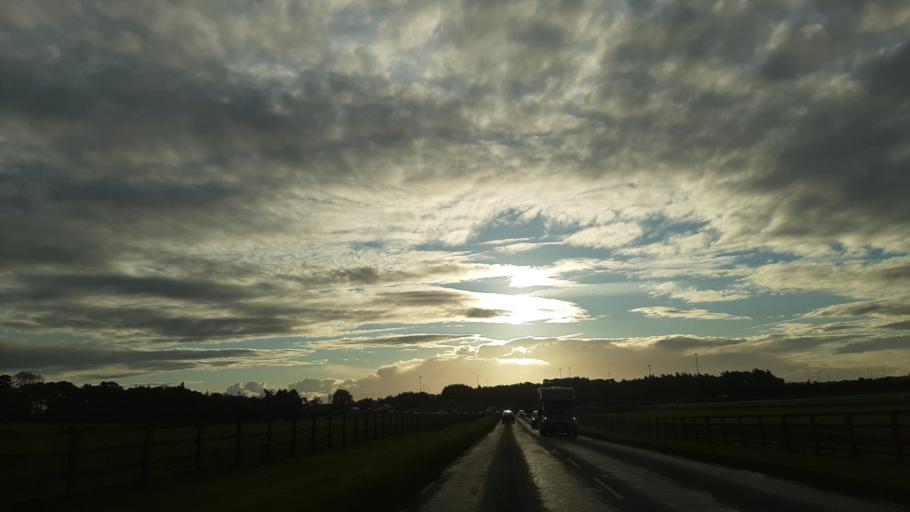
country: IE
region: Leinster
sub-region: Kildare
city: Athgarvan
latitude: 53.1645
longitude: -6.8327
